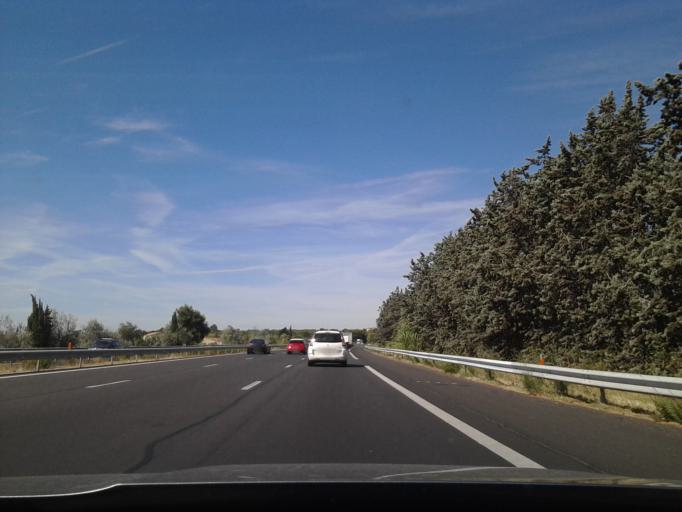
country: FR
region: Languedoc-Roussillon
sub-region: Departement de l'Aude
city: Fleury
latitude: 43.2347
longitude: 3.1362
